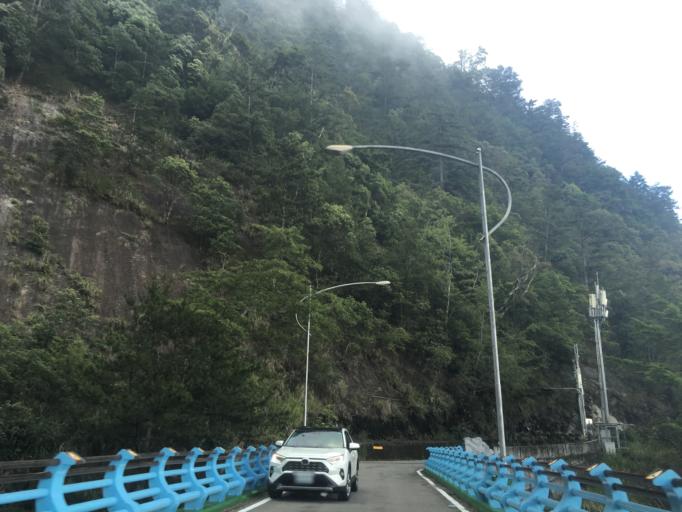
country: TW
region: Taiwan
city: Fengyuan
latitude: 24.2315
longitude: 120.9784
